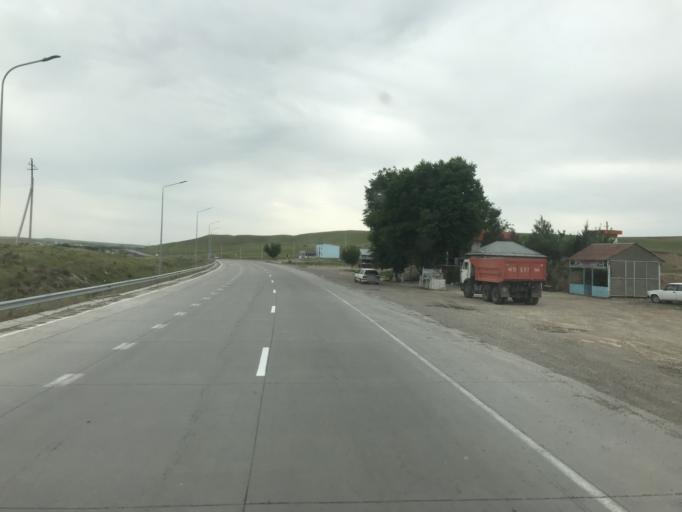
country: KZ
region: Ongtustik Qazaqstan
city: Qazyqurt
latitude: 41.9078
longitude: 69.4590
